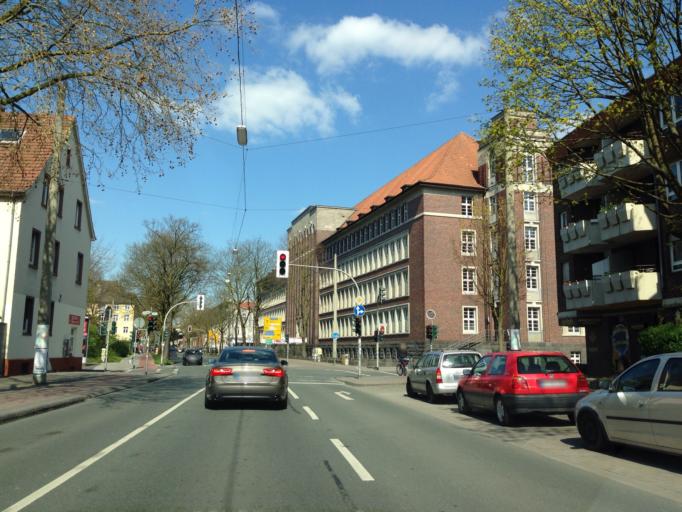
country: DE
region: North Rhine-Westphalia
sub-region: Regierungsbezirk Munster
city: Muenster
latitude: 51.9542
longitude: 7.6446
